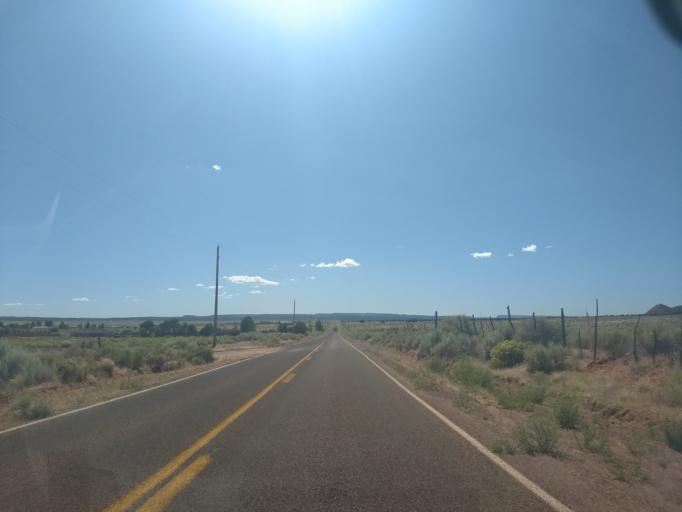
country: US
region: Arizona
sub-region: Mohave County
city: Colorado City
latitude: 36.9469
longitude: -112.9237
